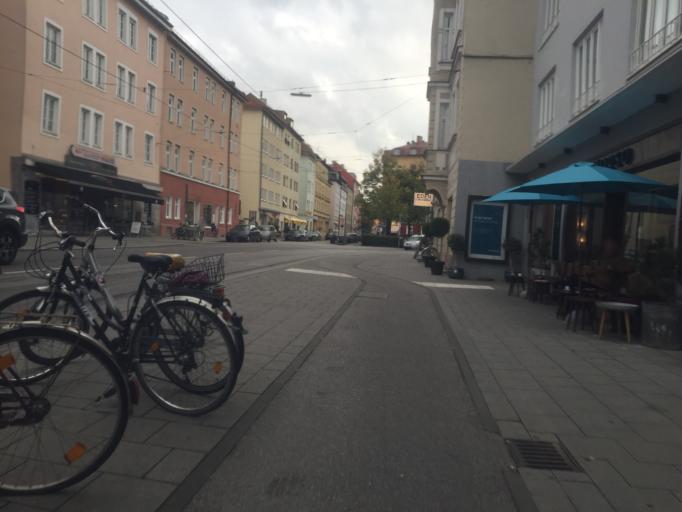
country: DE
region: Bavaria
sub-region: Upper Bavaria
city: Munich
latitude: 48.1549
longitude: 11.5753
